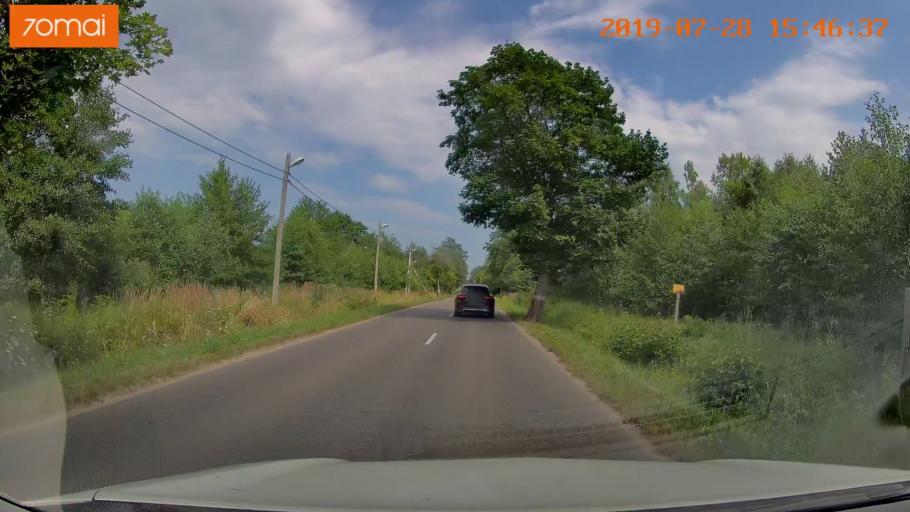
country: RU
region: Kaliningrad
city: Otradnoye
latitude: 54.9428
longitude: 20.0559
